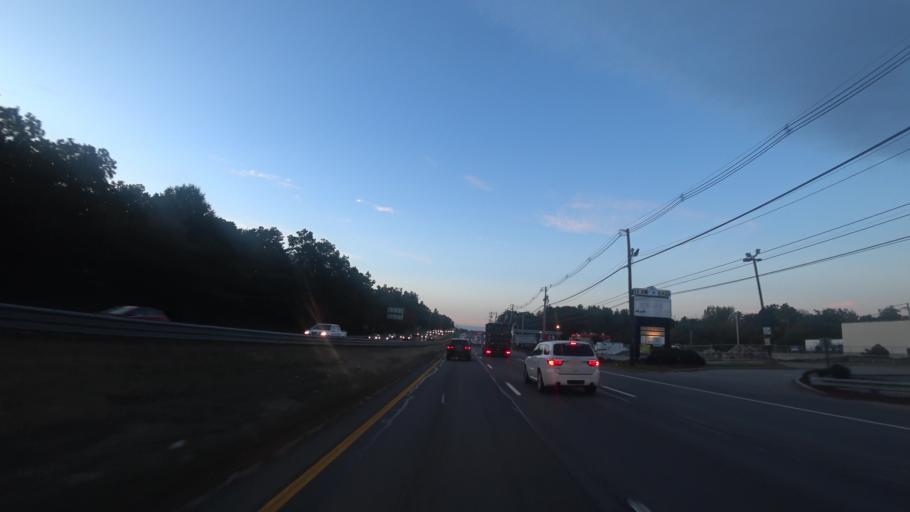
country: US
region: Massachusetts
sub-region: Essex County
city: Saugus
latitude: 42.5049
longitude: -71.0145
